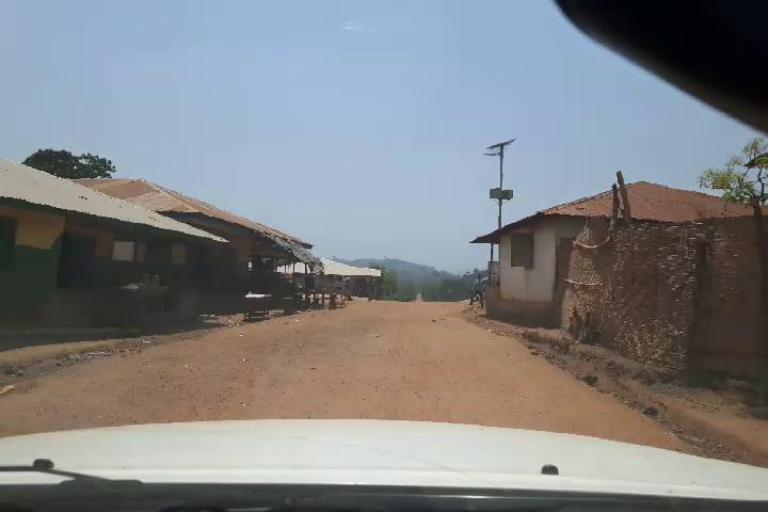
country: SL
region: Northern Province
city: Alikalia
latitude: 9.0626
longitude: -11.4892
